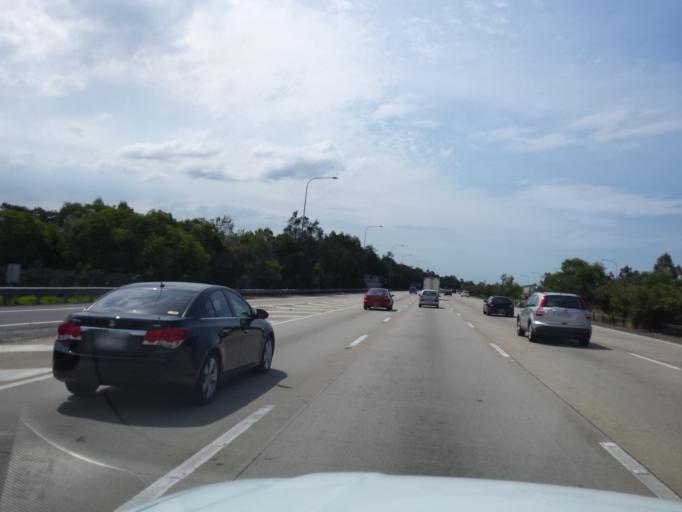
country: AU
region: Queensland
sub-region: Gold Coast
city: Oxenford
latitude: -27.9034
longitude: 153.3160
